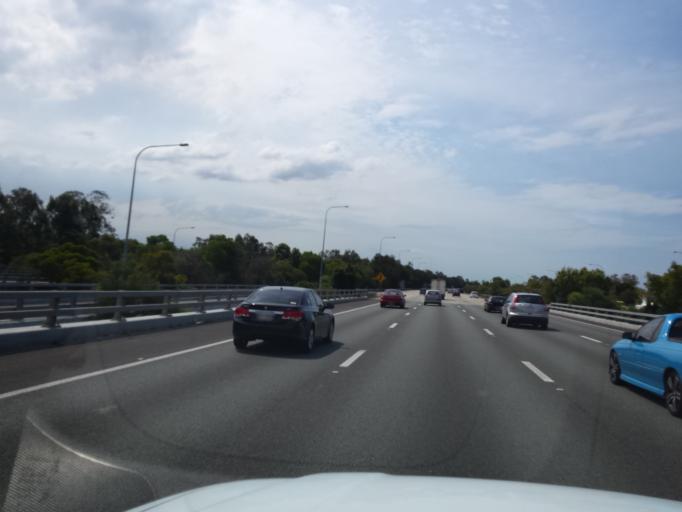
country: AU
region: Queensland
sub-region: Gold Coast
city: Oxenford
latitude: -27.9043
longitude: 153.3162
